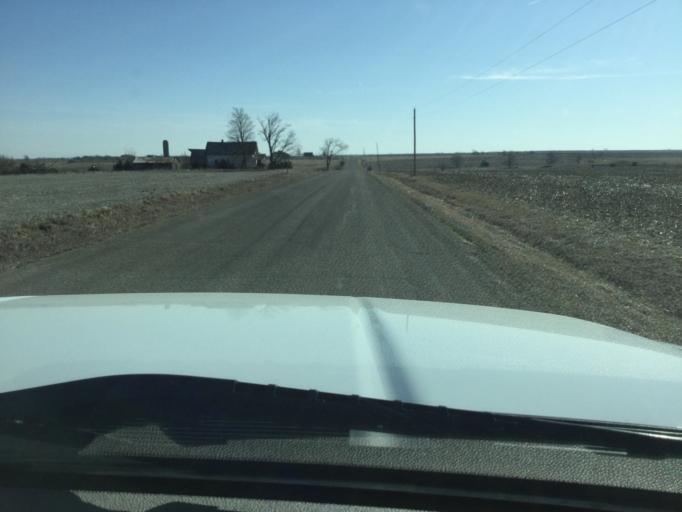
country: US
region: Kansas
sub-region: Brown County
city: Horton
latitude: 39.7256
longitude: -95.4604
